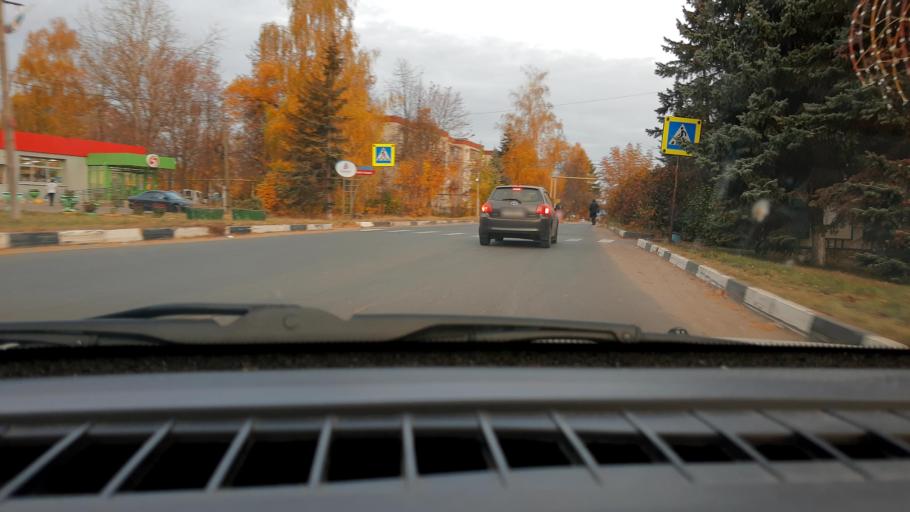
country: RU
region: Nizjnij Novgorod
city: Burevestnik
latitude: 56.2049
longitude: 43.8804
